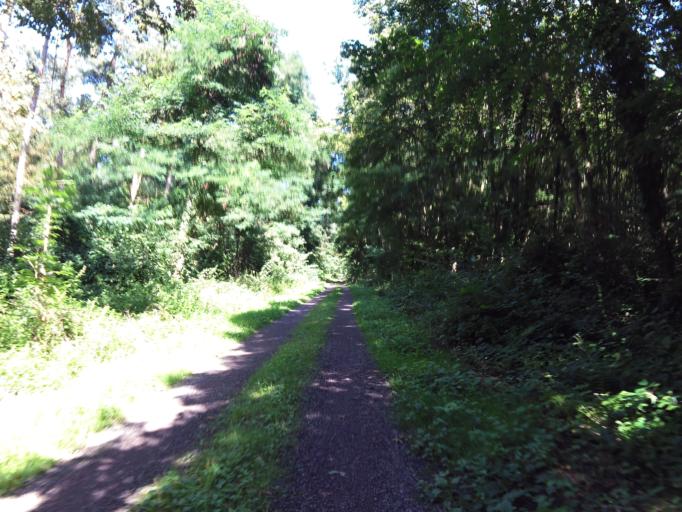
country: DE
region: Rheinland-Pfalz
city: Schwegenheim
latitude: 49.2869
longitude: 8.3105
